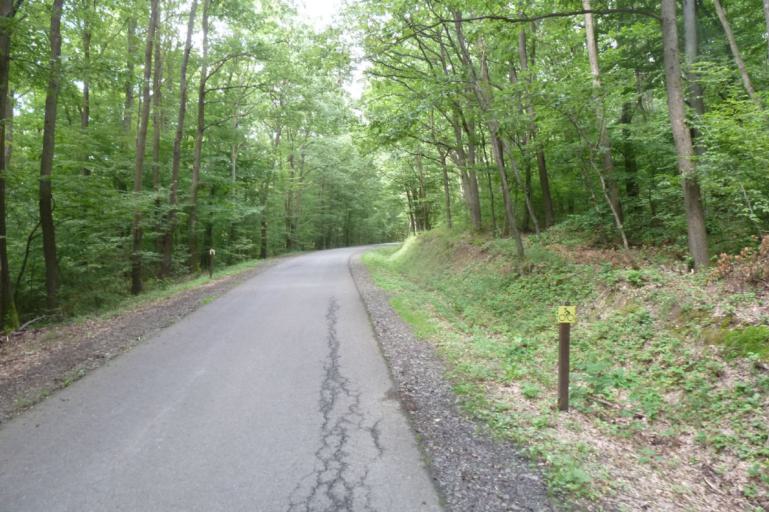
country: HU
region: Pest
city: Szob
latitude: 47.8930
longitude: 18.9245
